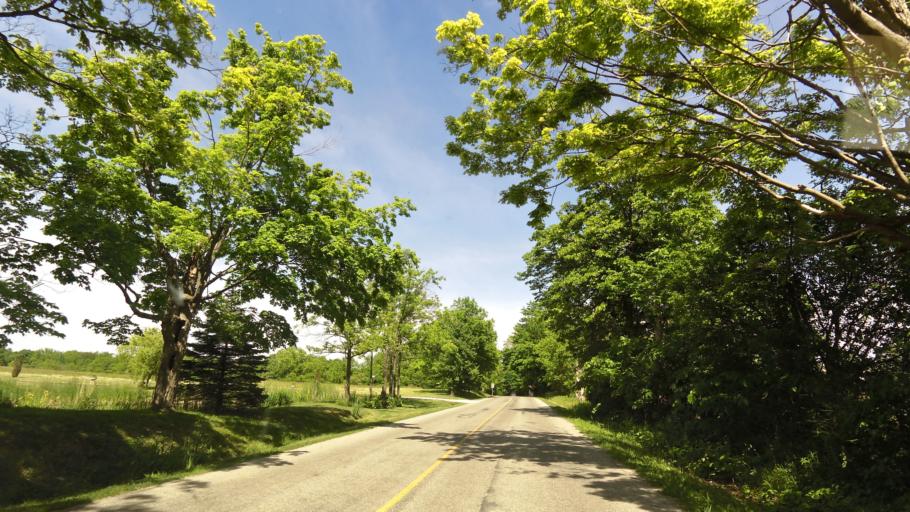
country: CA
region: Ontario
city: Norfolk County
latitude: 42.7553
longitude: -80.2640
